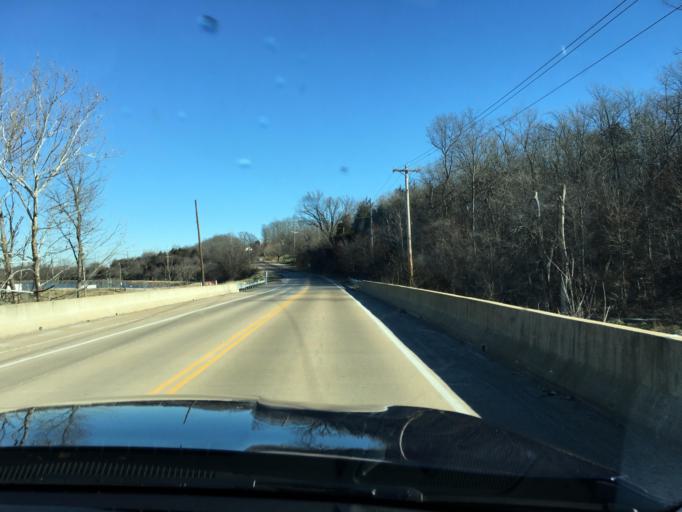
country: US
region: Missouri
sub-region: Jefferson County
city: De Soto
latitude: 38.1497
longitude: -90.5485
